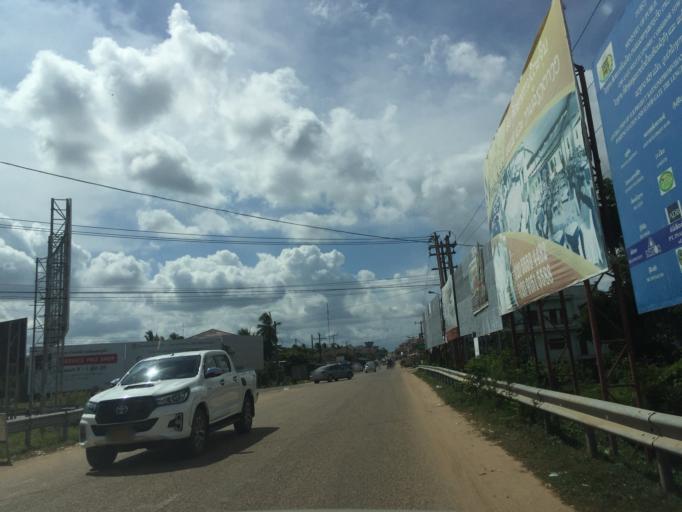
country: LA
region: Savannahkhet
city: Savannakhet
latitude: 16.5489
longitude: 104.7503
